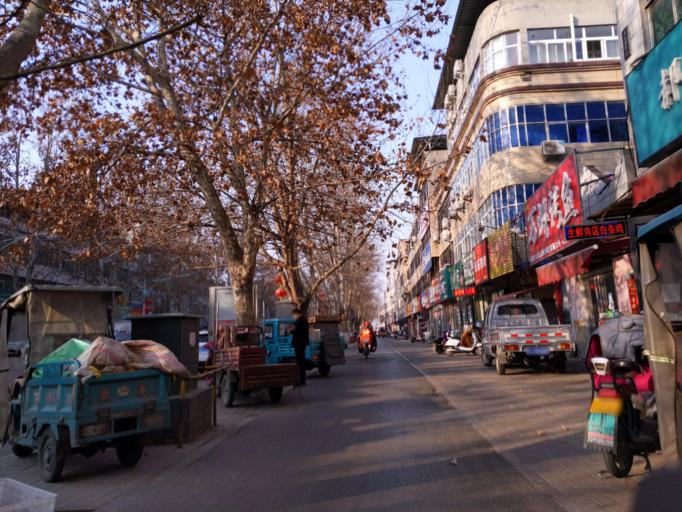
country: CN
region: Henan Sheng
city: Puyang
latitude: 35.7702
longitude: 115.0326
